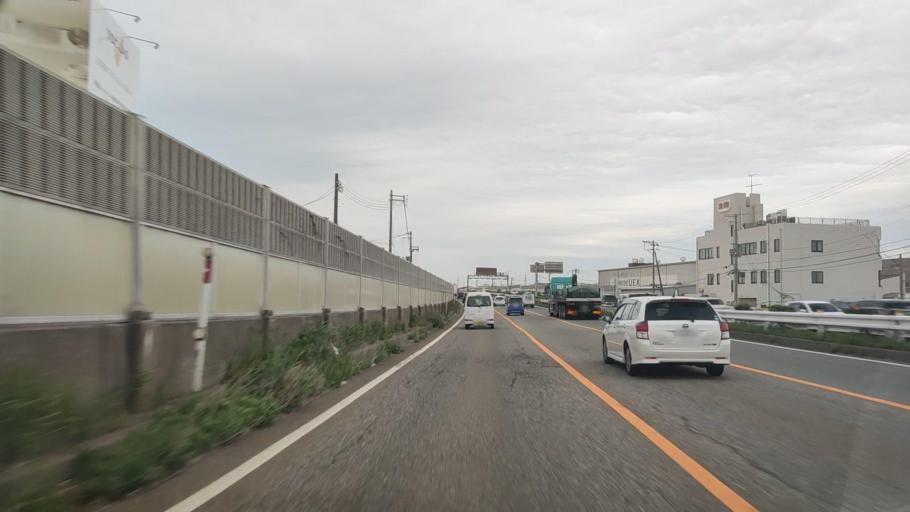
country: JP
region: Niigata
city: Kameda-honcho
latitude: 37.9080
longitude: 139.0873
